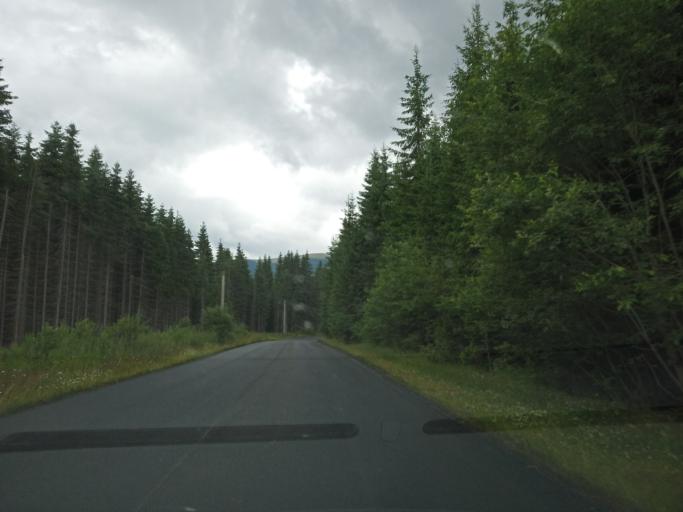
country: RO
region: Gorj
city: Novaci-Straini
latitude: 45.4225
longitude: 23.6953
